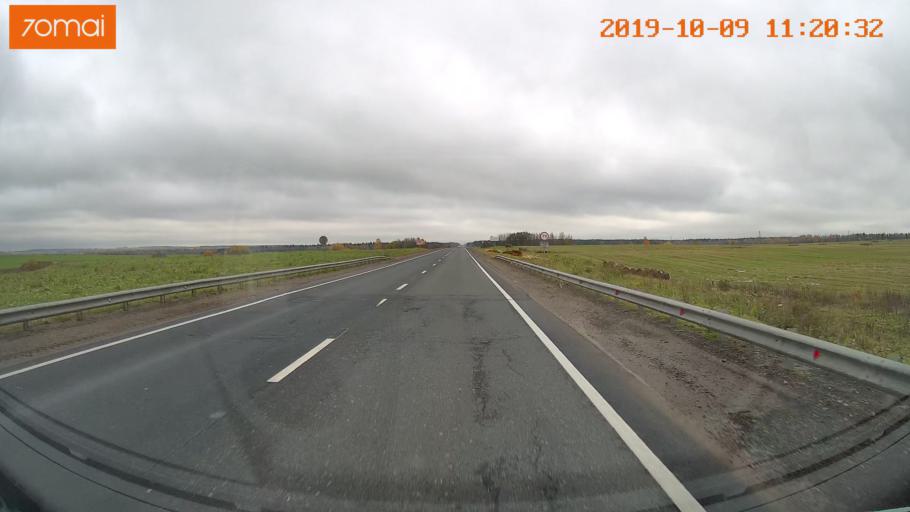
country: RU
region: Vologda
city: Vologda
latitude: 59.1487
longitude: 39.9395
